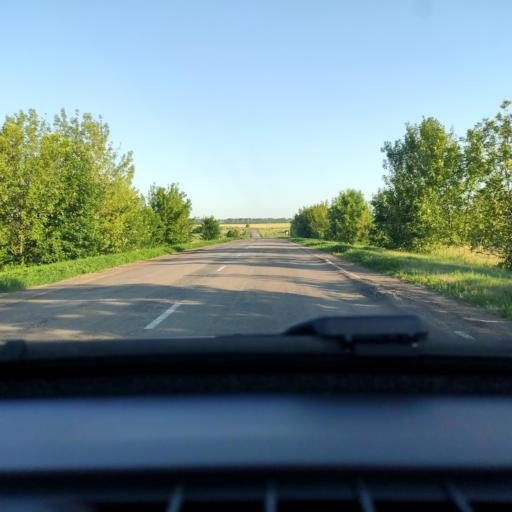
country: RU
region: Voronezj
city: Kashirskoye
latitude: 51.5028
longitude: 39.8327
